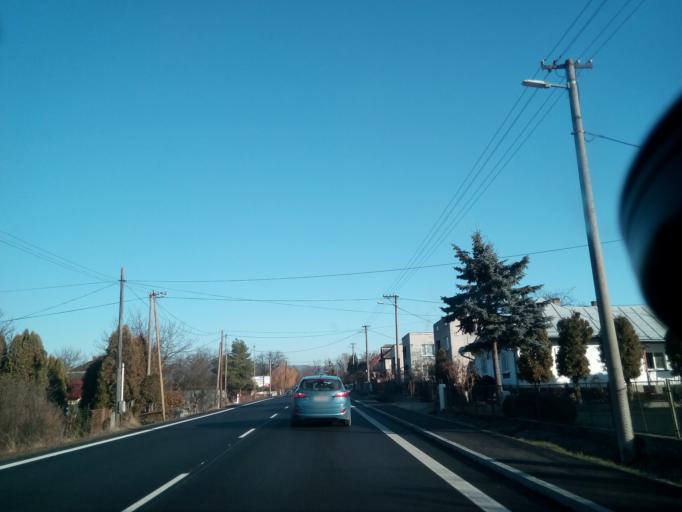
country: SK
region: Kosicky
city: Secovce
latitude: 48.7361
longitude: 21.4679
